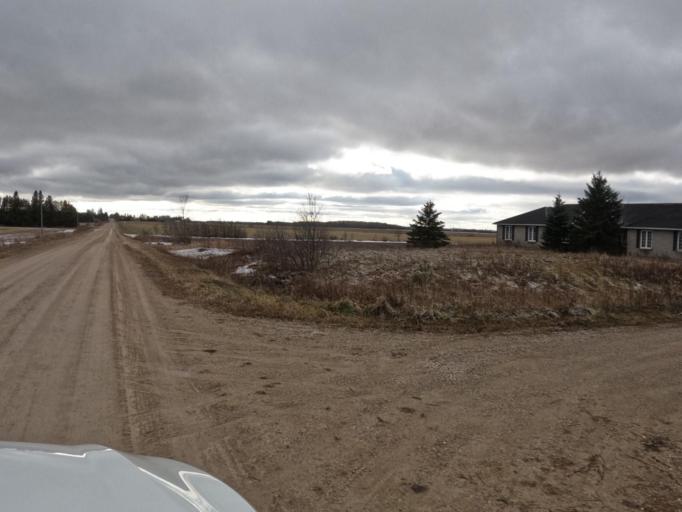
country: CA
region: Ontario
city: Shelburne
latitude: 44.0259
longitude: -80.3702
